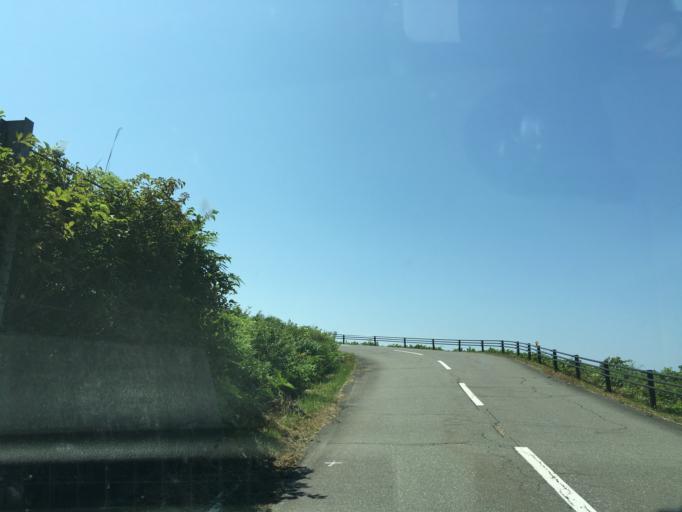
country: JP
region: Akita
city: Tenno
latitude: 39.9333
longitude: 139.8721
